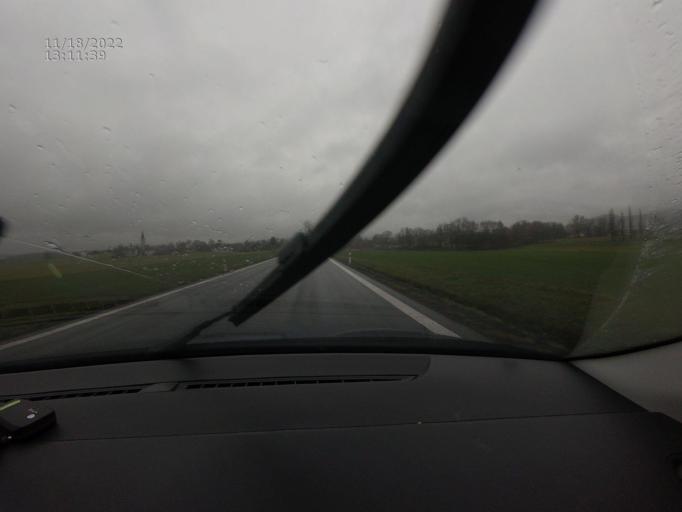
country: CZ
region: Plzensky
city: Horazd'ovice
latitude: 49.3257
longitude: 13.5896
